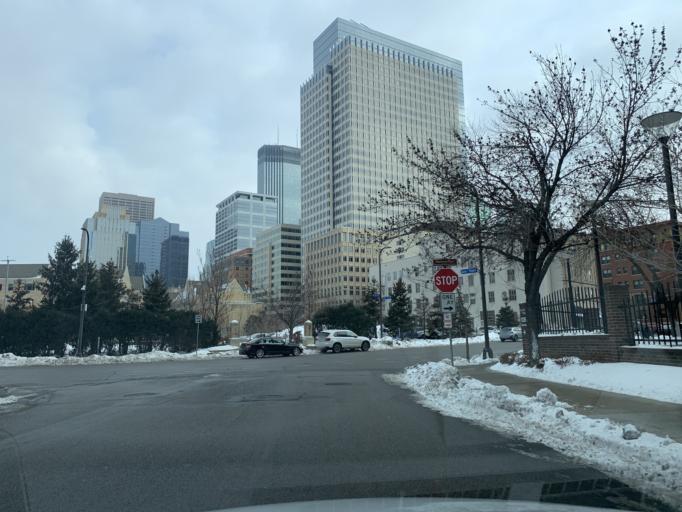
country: US
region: Minnesota
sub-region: Hennepin County
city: Minneapolis
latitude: 44.9728
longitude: -93.2792
